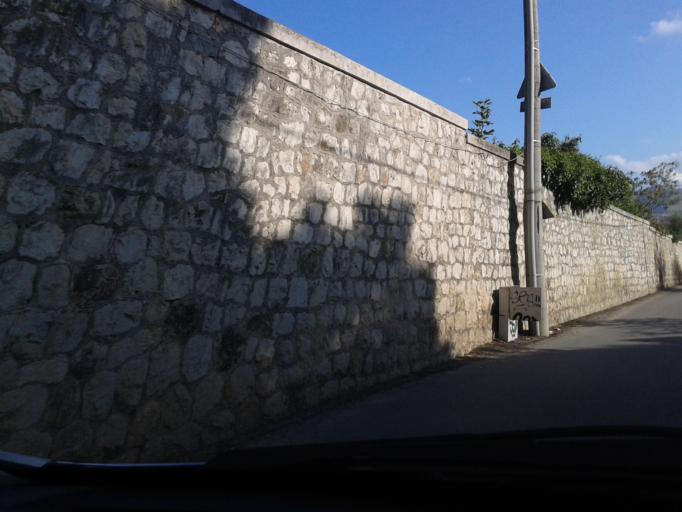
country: IT
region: Sicily
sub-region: Palermo
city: Monreale
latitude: 38.1027
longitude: 13.3157
